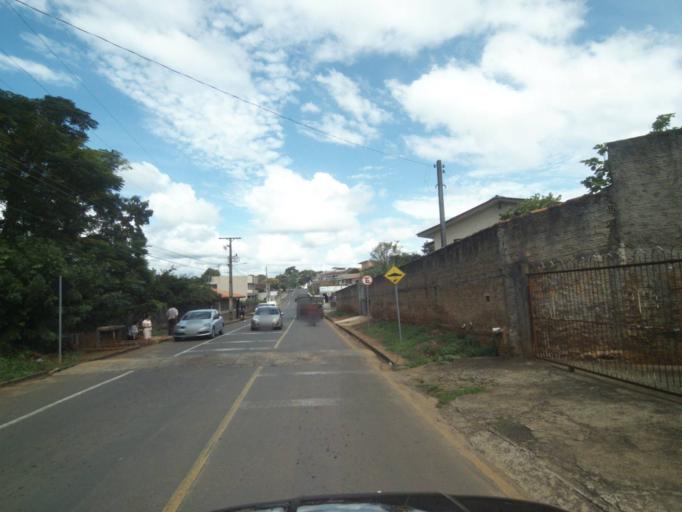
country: BR
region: Parana
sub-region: Telemaco Borba
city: Telemaco Borba
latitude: -24.3212
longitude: -50.6283
